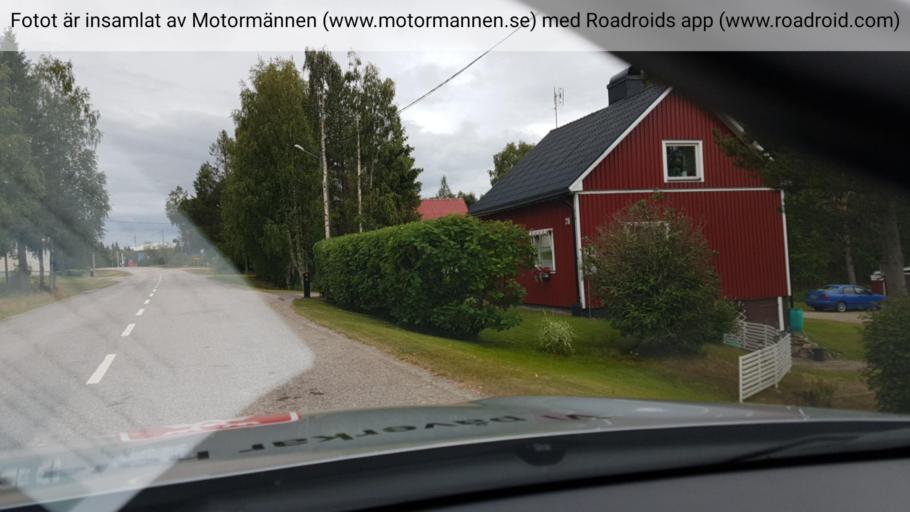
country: SE
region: Norrbotten
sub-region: Overkalix Kommun
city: OEverkalix
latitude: 66.7888
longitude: 22.9188
